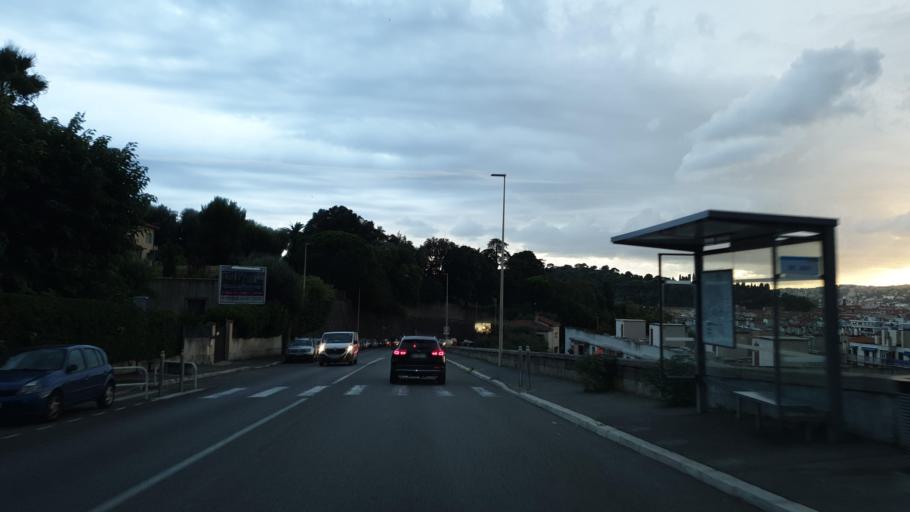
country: FR
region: Provence-Alpes-Cote d'Azur
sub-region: Departement des Alpes-Maritimes
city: Villefranche-sur-Mer
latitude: 43.7021
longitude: 7.2933
